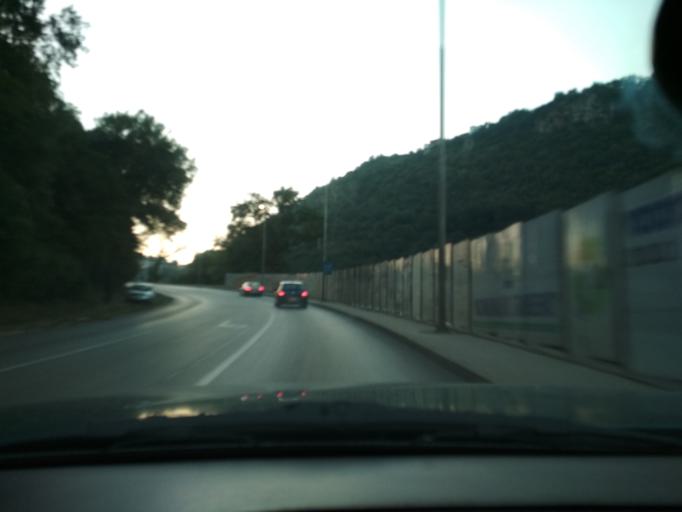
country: ME
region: Herceg Novi
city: Herceg-Novi
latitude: 42.4555
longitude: 18.5523
